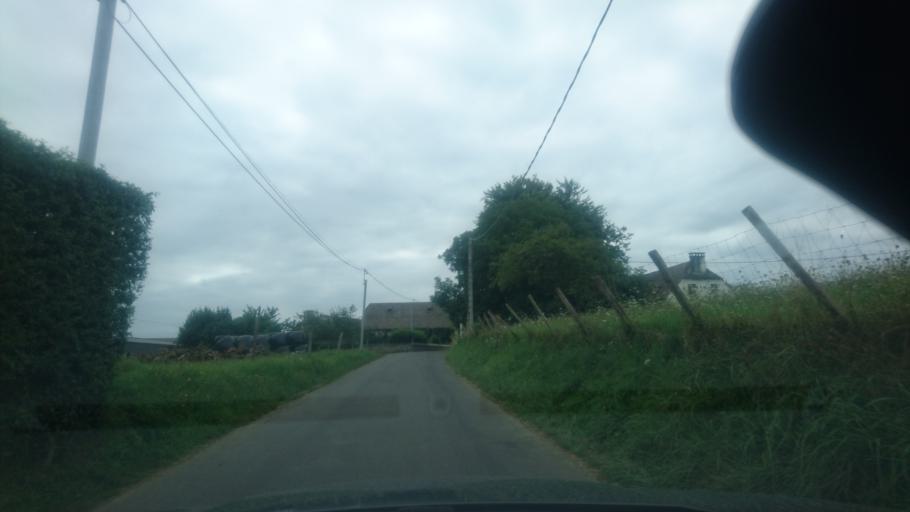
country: FR
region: Midi-Pyrenees
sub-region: Departement des Hautes-Pyrenees
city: Horgues
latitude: 43.1210
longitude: 0.0664
